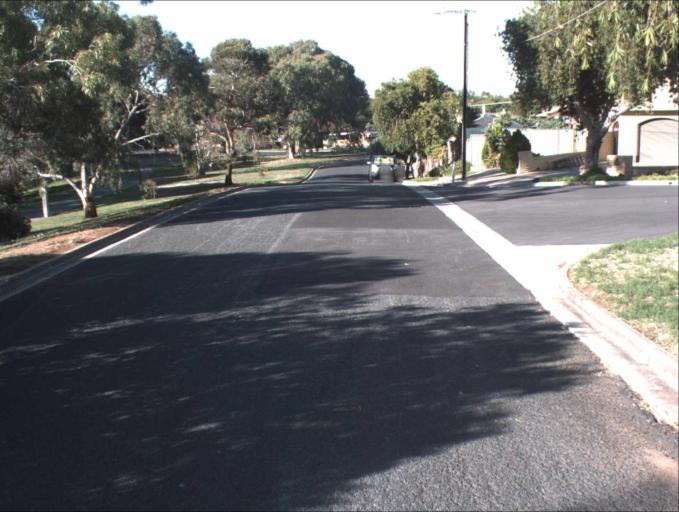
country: AU
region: South Australia
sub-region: Port Adelaide Enfield
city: Klemzig
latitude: -34.8752
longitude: 138.6470
